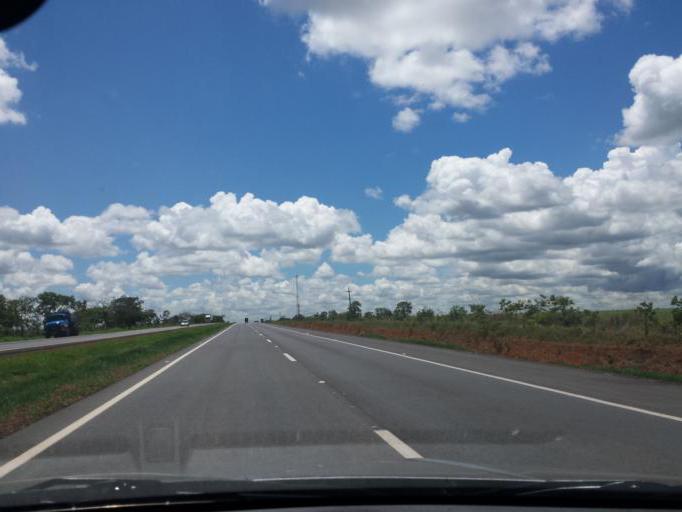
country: BR
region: Goias
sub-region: Cristalina
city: Cristalina
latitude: -16.6716
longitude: -47.7118
